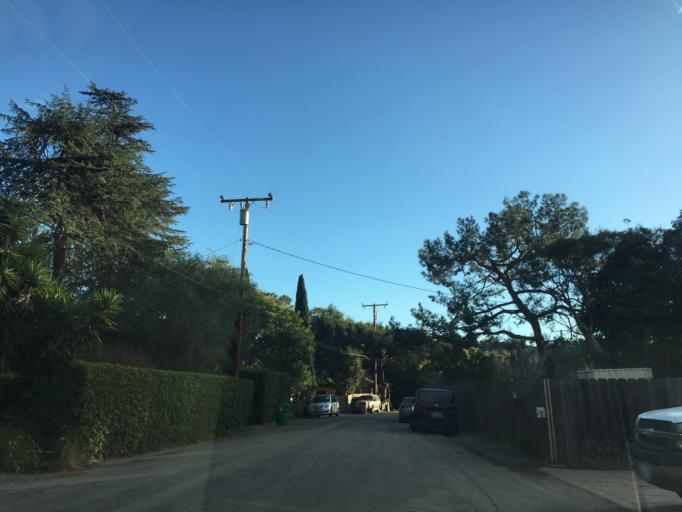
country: US
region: California
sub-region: Santa Barbara County
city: Goleta
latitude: 34.4393
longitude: -119.7724
